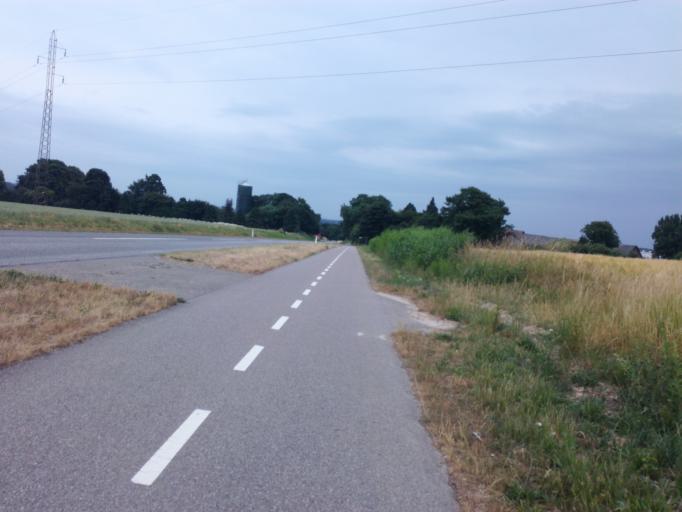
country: DK
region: South Denmark
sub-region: Vejle Kommune
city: Borkop
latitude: 55.6604
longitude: 9.6312
